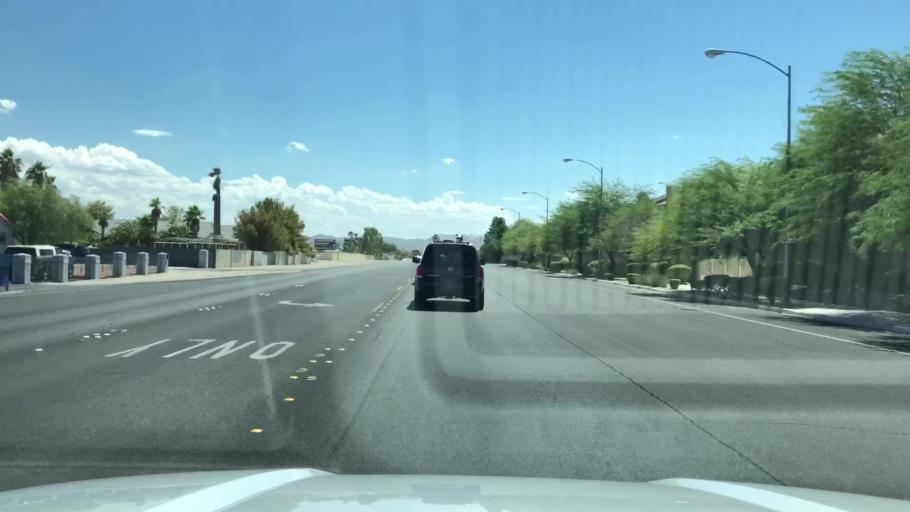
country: US
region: Nevada
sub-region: Clark County
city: Enterprise
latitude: 36.0492
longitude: -115.2080
